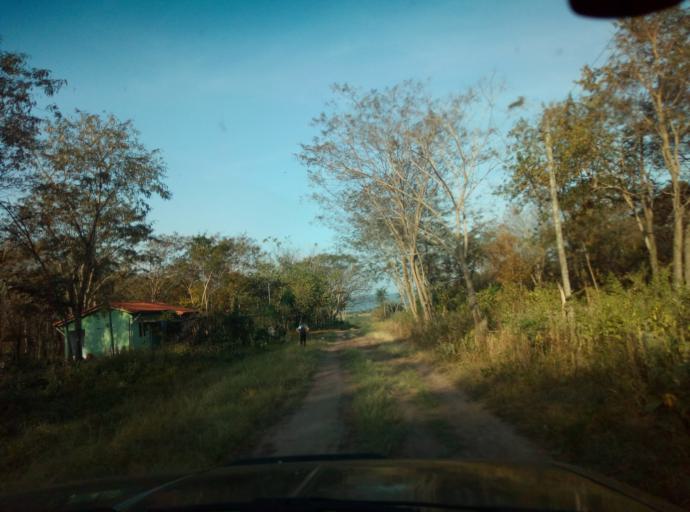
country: PY
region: Caaguazu
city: Doctor Cecilio Baez
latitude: -25.2000
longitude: -56.1317
